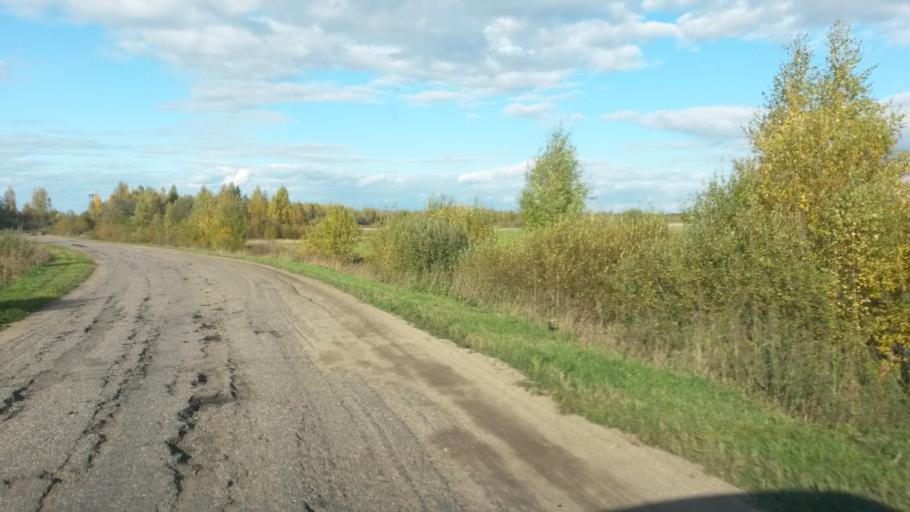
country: RU
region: Jaroslavl
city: Tunoshna
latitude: 57.5254
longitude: 40.0111
